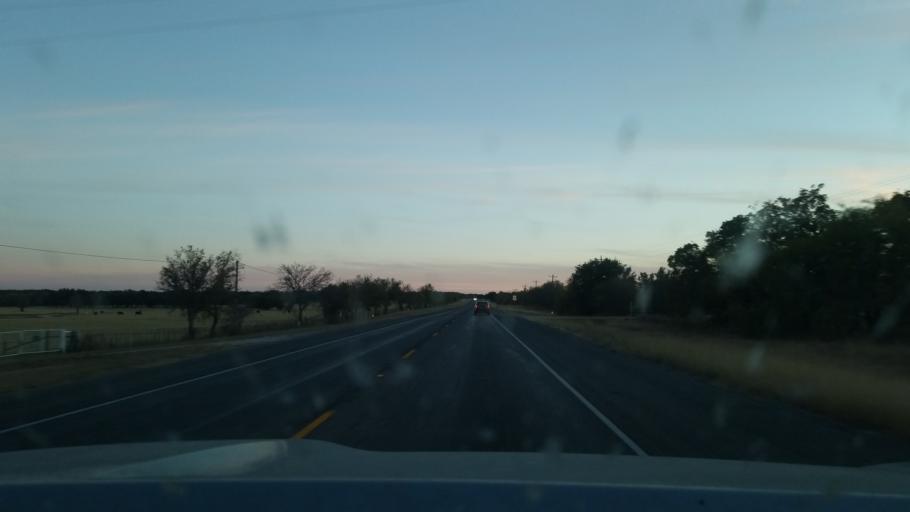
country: US
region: Texas
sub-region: Stephens County
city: Breckenridge
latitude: 32.5922
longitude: -98.8986
